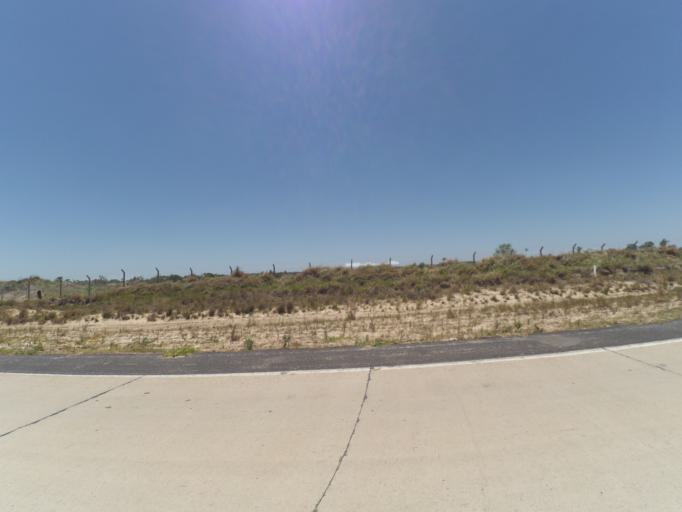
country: BO
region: Santa Cruz
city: Santa Cruz de la Sierra
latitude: -17.7942
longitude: -63.2759
